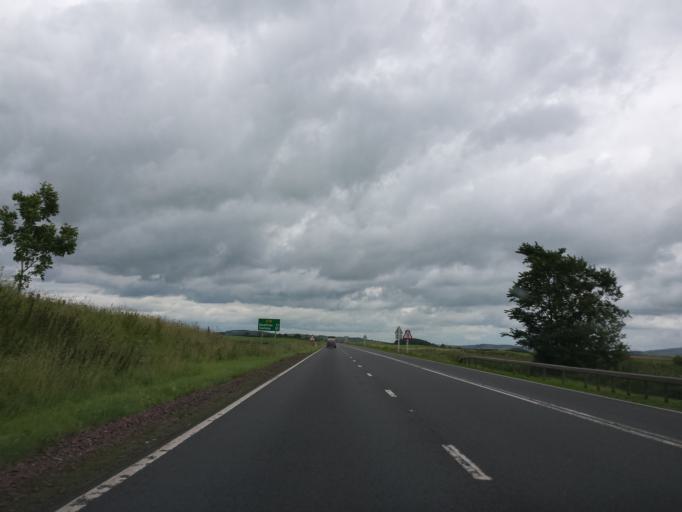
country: GB
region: Scotland
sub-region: Dumfries and Galloway
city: Castle Douglas
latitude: 54.9596
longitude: -3.9153
